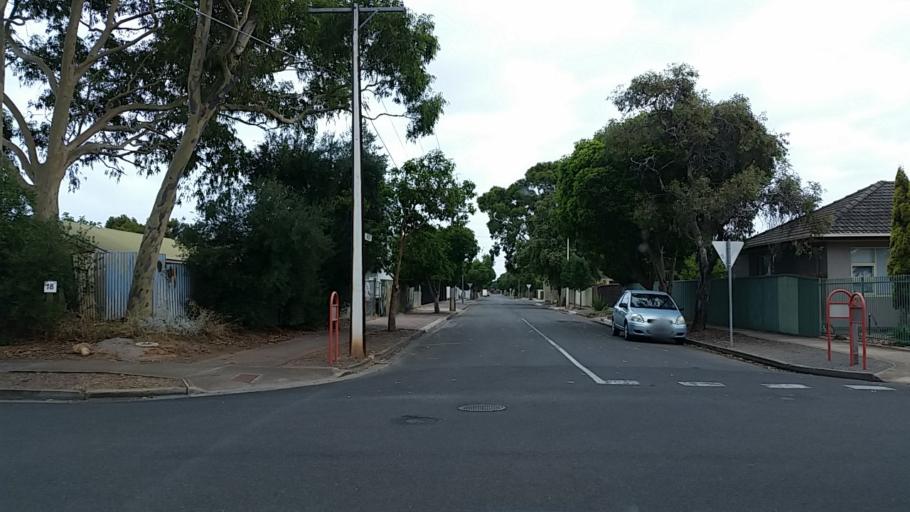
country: AU
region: South Australia
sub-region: Holdfast Bay
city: North Brighton
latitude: -35.0021
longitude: 138.5246
